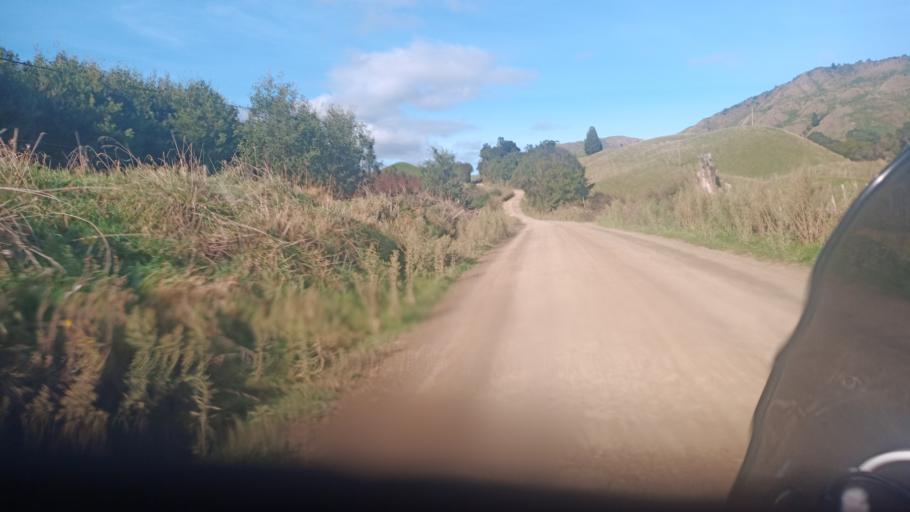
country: NZ
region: Bay of Plenty
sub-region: Opotiki District
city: Opotiki
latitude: -38.4220
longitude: 177.5584
